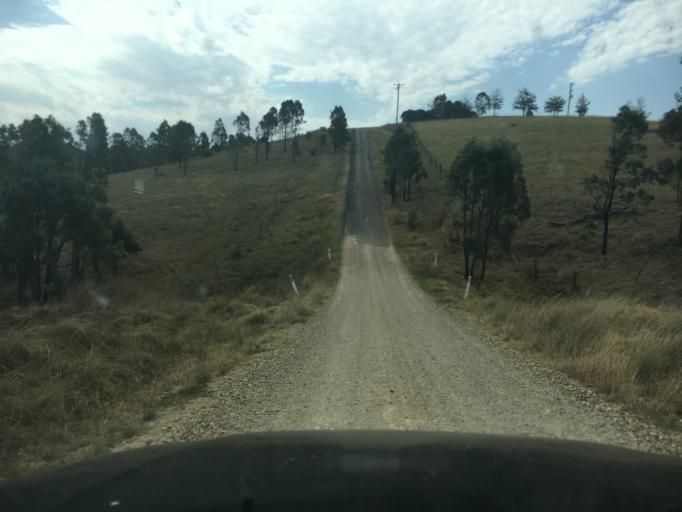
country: AU
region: New South Wales
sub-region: Cessnock
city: Branxton
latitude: -32.5032
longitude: 151.3164
